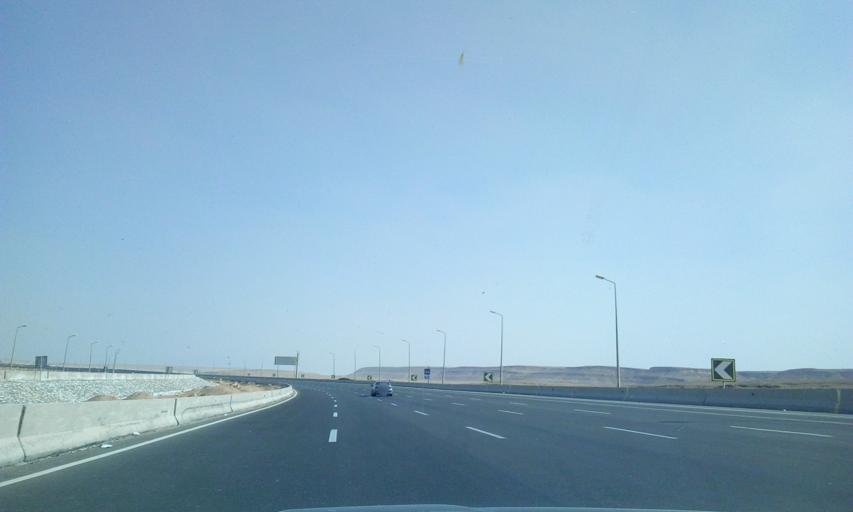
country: EG
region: As Suways
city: Ain Sukhna
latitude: 29.7850
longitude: 31.9032
